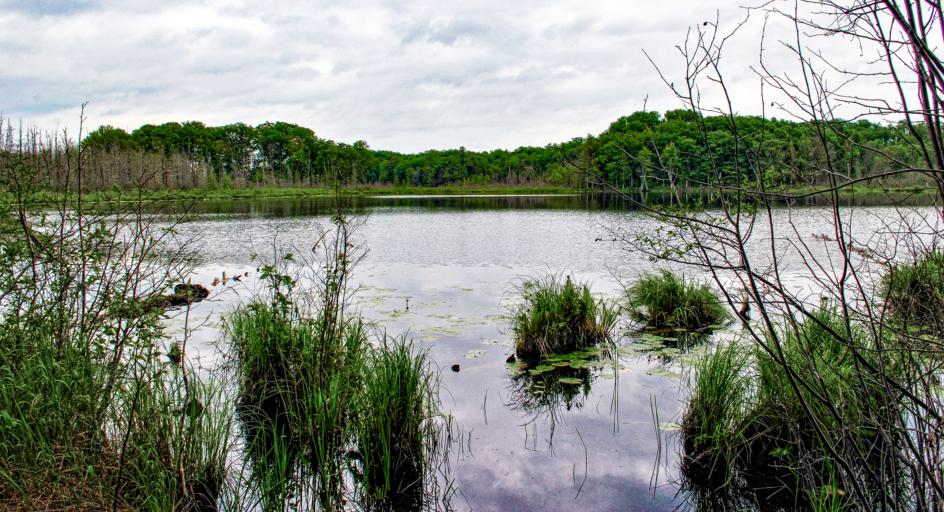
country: US
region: Wisconsin
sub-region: Chippewa County
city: Bloomer
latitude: 45.2154
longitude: -91.3559
